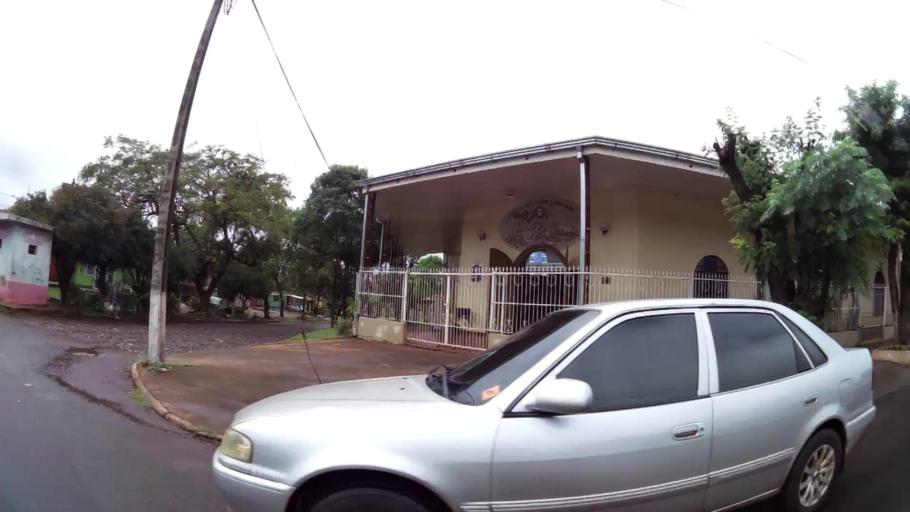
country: PY
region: Alto Parana
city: Ciudad del Este
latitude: -25.5055
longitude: -54.6596
